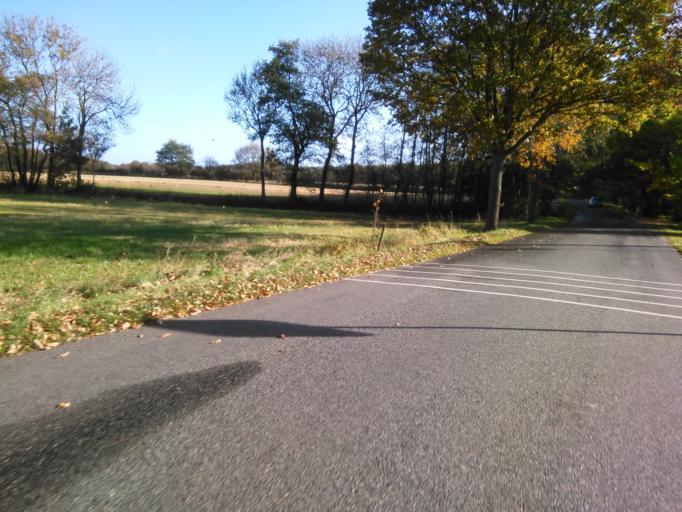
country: DK
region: Central Jutland
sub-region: Arhus Kommune
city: Beder
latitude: 56.0753
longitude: 10.2186
